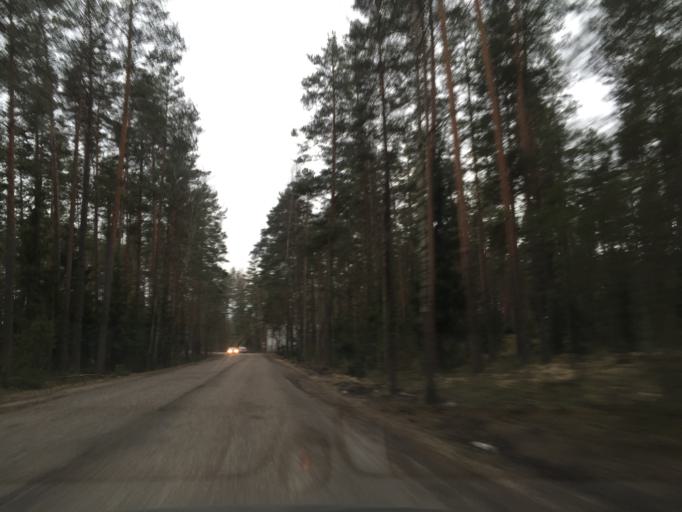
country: LV
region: Garkalne
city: Garkalne
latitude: 56.9573
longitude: 24.4364
